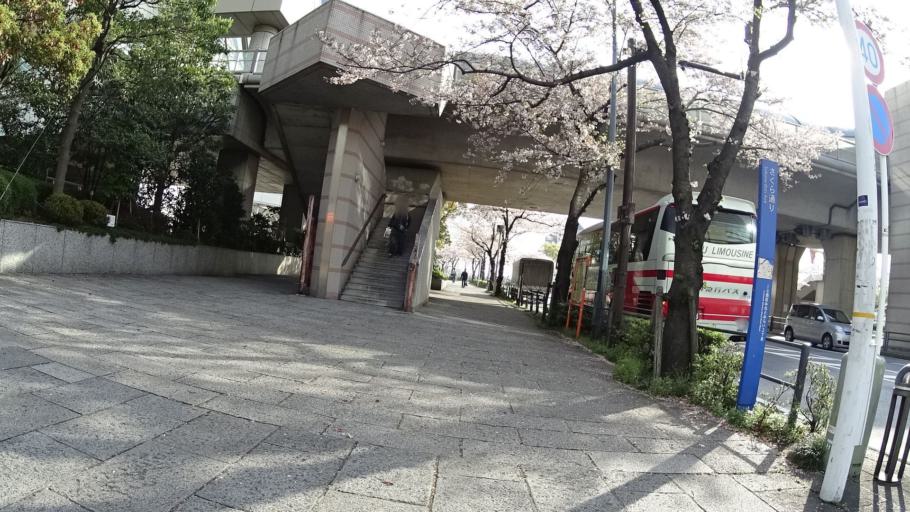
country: JP
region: Kanagawa
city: Yokohama
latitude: 35.4538
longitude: 139.6312
